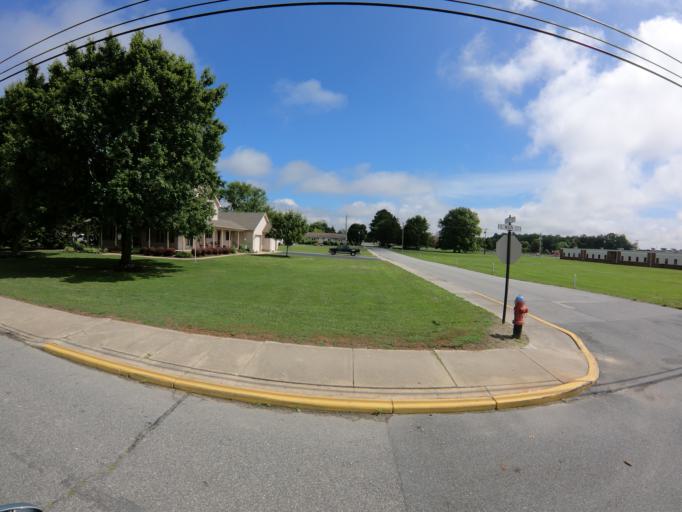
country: US
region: Delaware
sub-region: Kent County
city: Felton
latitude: 39.0075
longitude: -75.5721
